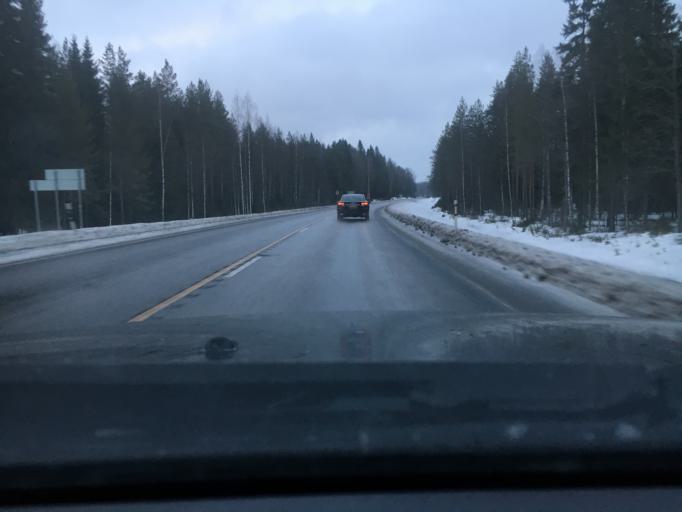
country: FI
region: Central Finland
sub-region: Jyvaeskylae
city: Hankasalmi
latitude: 62.3655
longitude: 26.5745
